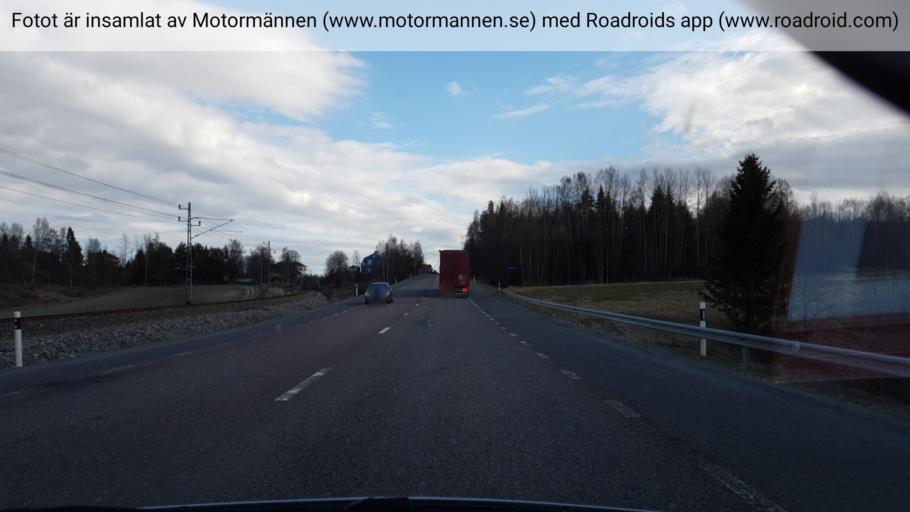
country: SE
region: Vaesternorrland
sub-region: Kramfors Kommun
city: Kramfors
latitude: 62.8931
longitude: 17.8507
